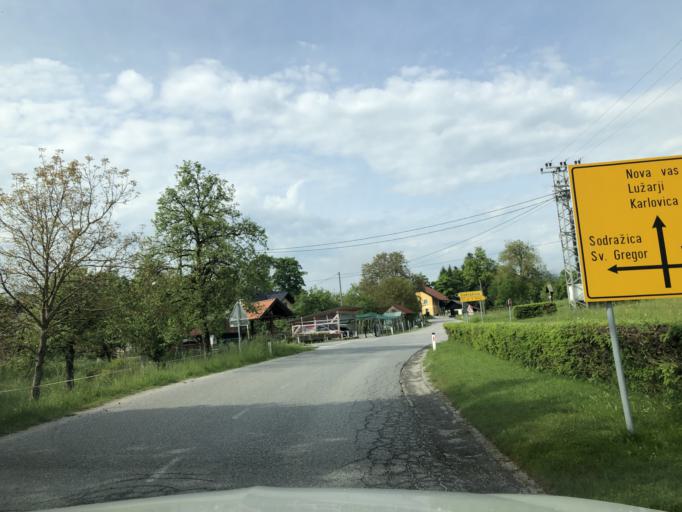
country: SI
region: Velike Lasce
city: Velike Lasce
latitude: 45.8095
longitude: 14.6263
